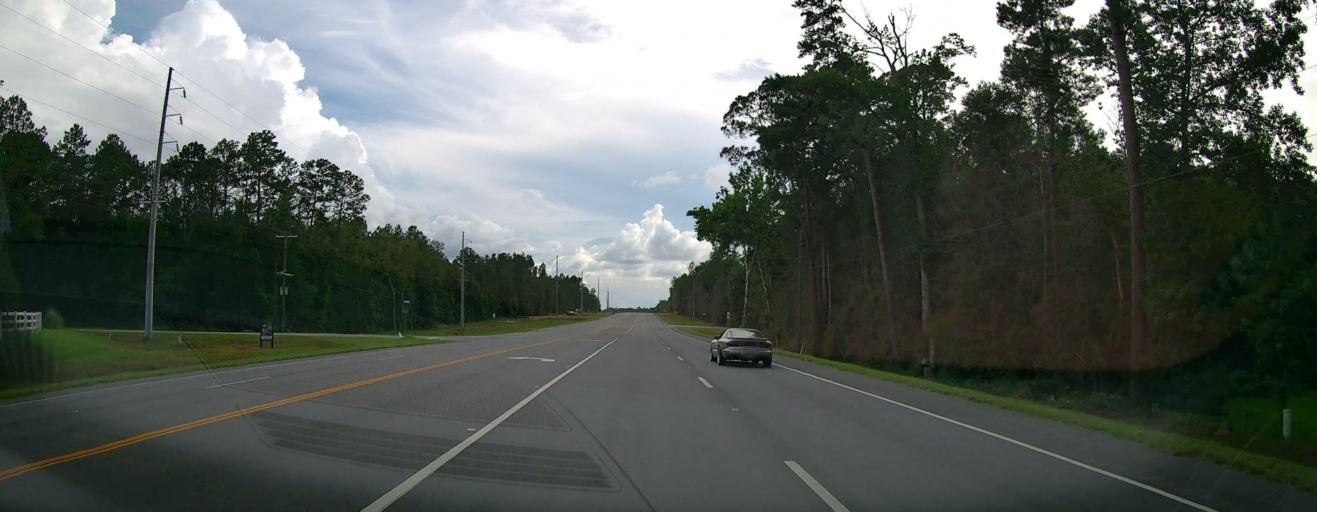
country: US
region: Georgia
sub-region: Wayne County
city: Jesup
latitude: 31.4728
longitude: -82.0362
